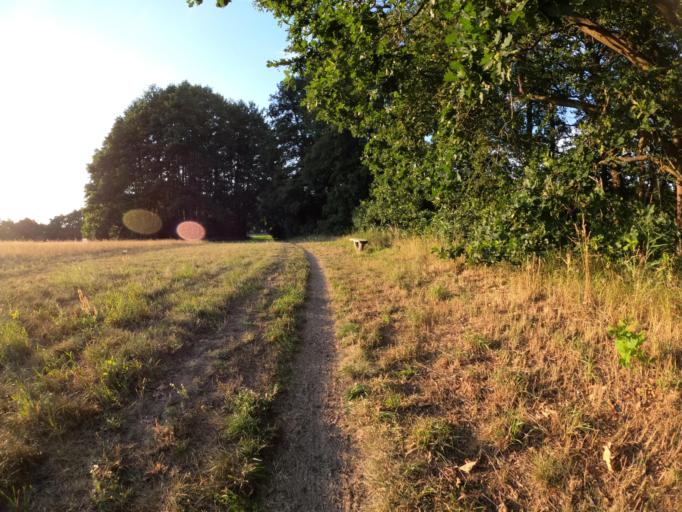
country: DE
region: Brandenburg
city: Templin
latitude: 53.1365
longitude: 13.5421
